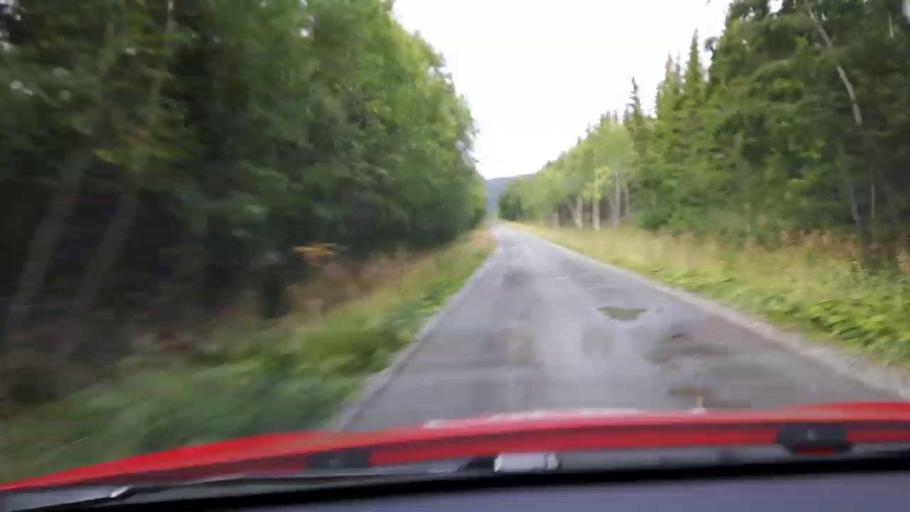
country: SE
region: Jaemtland
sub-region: Are Kommun
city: Are
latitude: 63.8054
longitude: 13.1124
